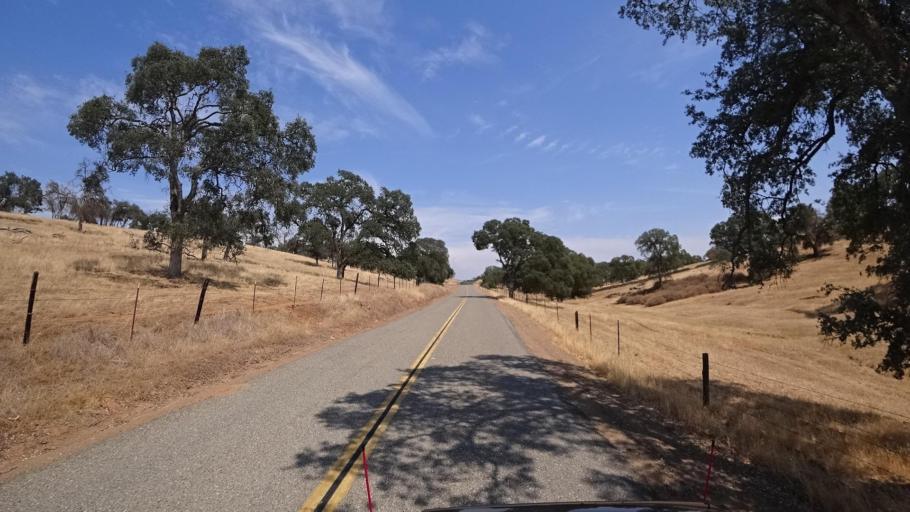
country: US
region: California
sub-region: Merced County
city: Planada
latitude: 37.5202
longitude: -120.2313
